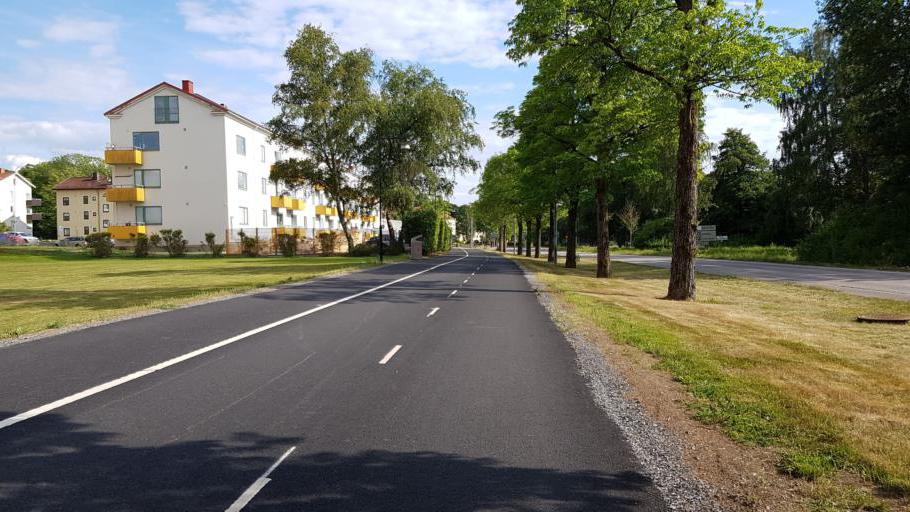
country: SE
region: Vaestra Goetaland
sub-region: Molndal
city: Moelndal
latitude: 57.7076
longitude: 12.0242
